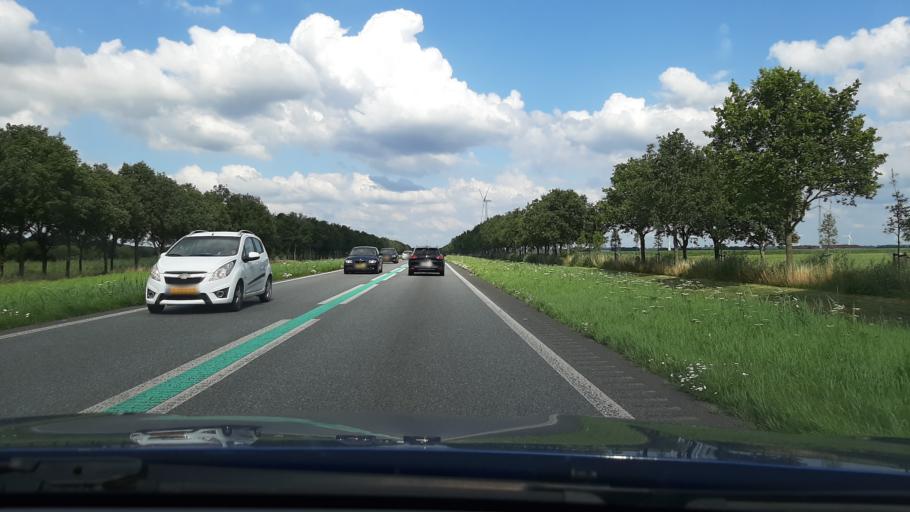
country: NL
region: Utrecht
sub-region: Gemeente Bunschoten
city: Spakenburg
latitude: 52.3105
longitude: 5.3624
